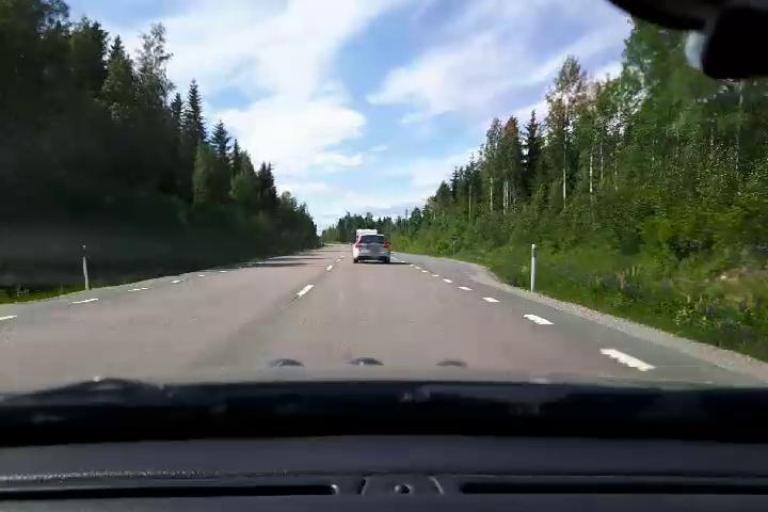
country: SE
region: Gaevleborg
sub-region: Bollnas Kommun
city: Kilafors
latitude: 61.2862
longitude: 16.5137
